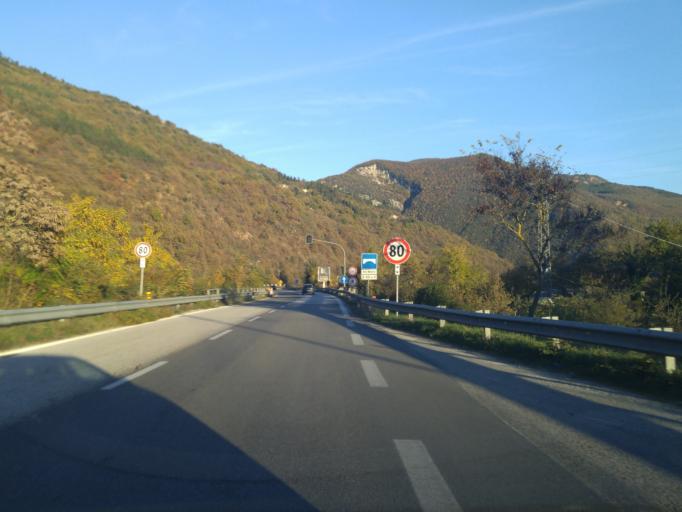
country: IT
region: The Marches
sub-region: Provincia di Pesaro e Urbino
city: Acqualagna
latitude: 43.6384
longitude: 12.6971
